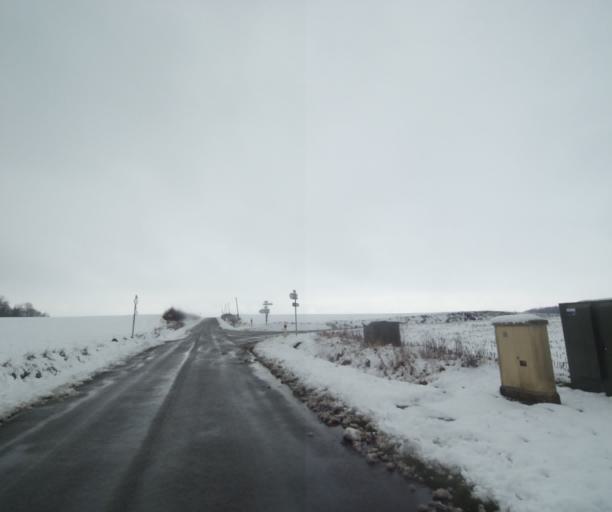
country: FR
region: Champagne-Ardenne
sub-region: Departement de la Haute-Marne
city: Montier-en-Der
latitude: 48.4633
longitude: 4.8246
